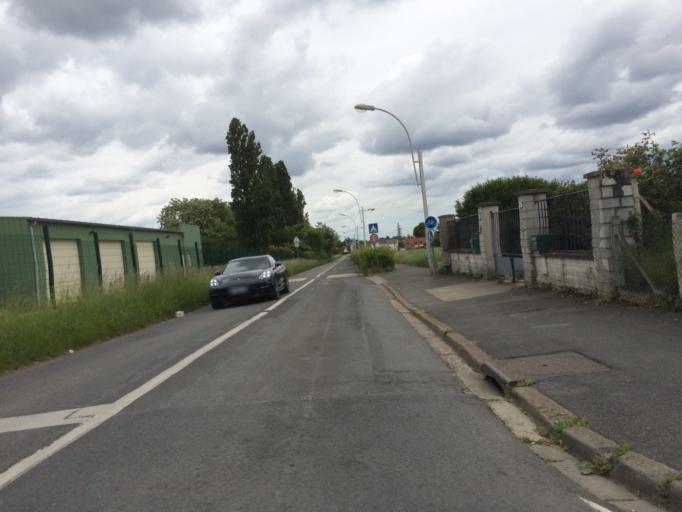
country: FR
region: Ile-de-France
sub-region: Departement de l'Essonne
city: Ballainvilliers
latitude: 48.6810
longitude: 2.2869
